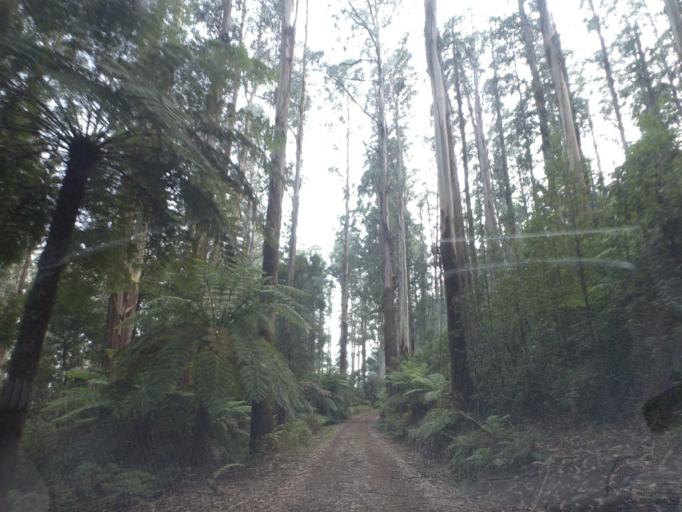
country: AU
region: Victoria
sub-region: Yarra Ranges
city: Healesville
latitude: -37.5729
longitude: 145.5189
